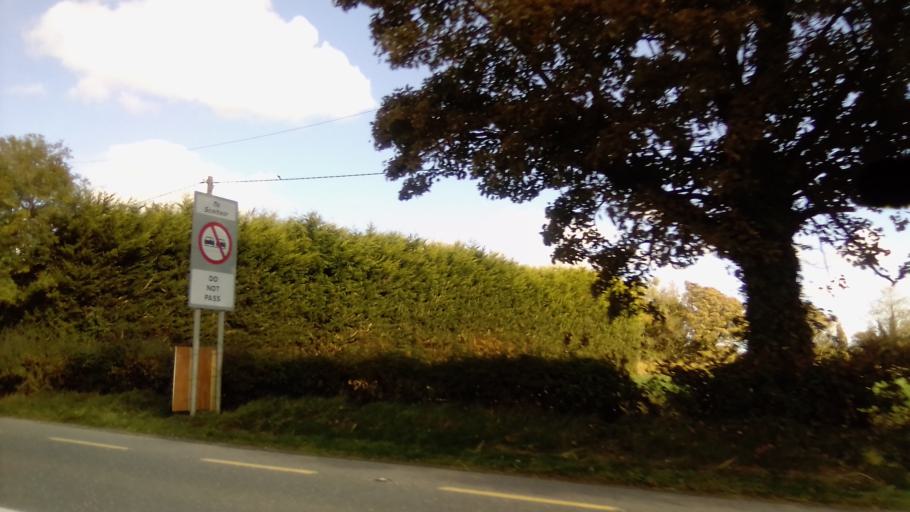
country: IE
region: Leinster
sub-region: An Mhi
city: Ratoath
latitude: 53.5516
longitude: -6.4353
